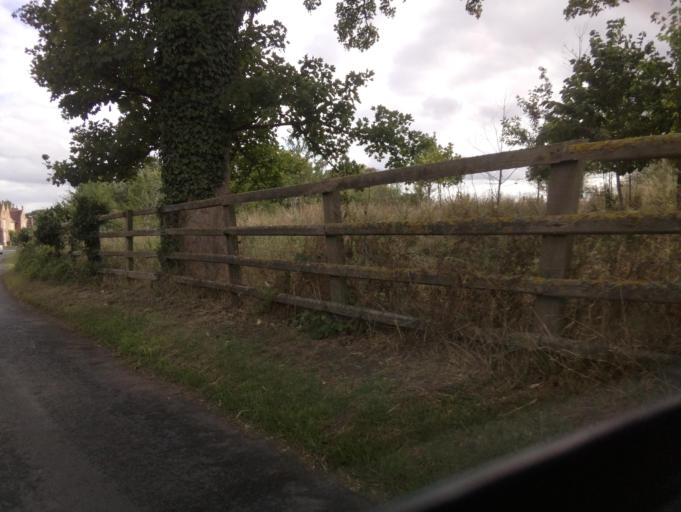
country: GB
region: England
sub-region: Leicestershire
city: Loughborough
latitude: 52.7944
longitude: -1.1955
